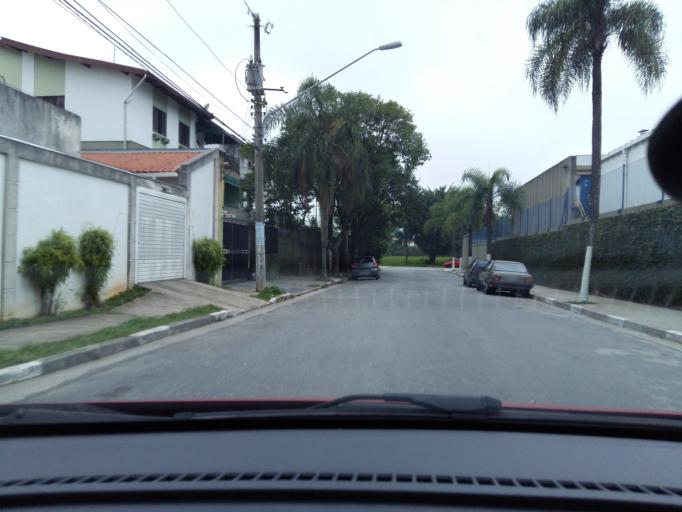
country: BR
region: Sao Paulo
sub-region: Sao Caetano Do Sul
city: Sao Caetano do Sul
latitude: -23.6397
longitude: -46.5935
